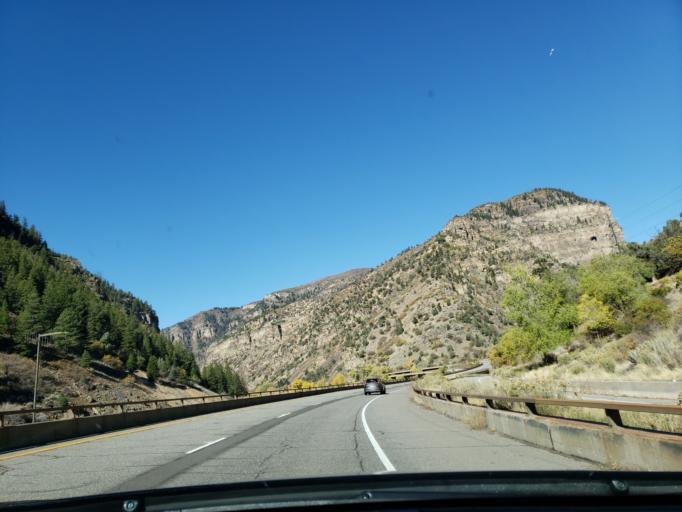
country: US
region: Colorado
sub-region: Garfield County
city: Glenwood Springs
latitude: 39.5578
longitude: -107.2461
